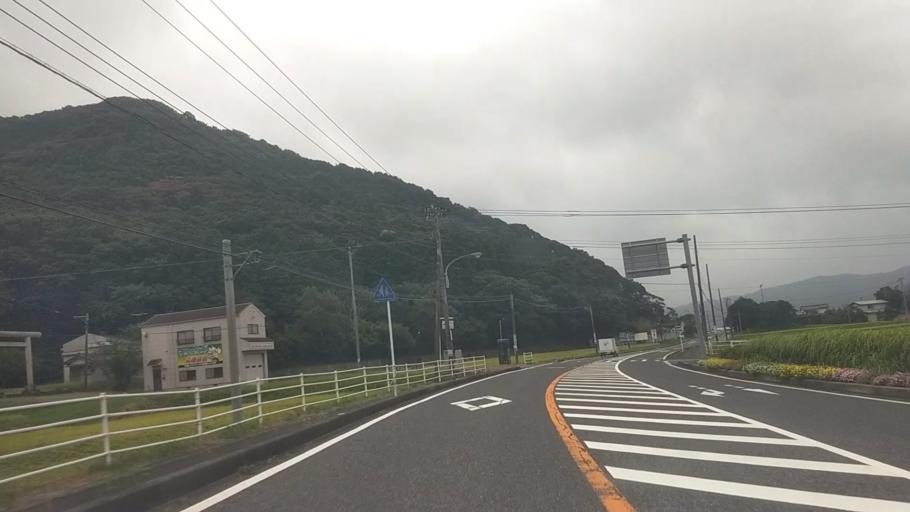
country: JP
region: Chiba
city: Kawaguchi
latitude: 35.1321
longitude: 140.0788
